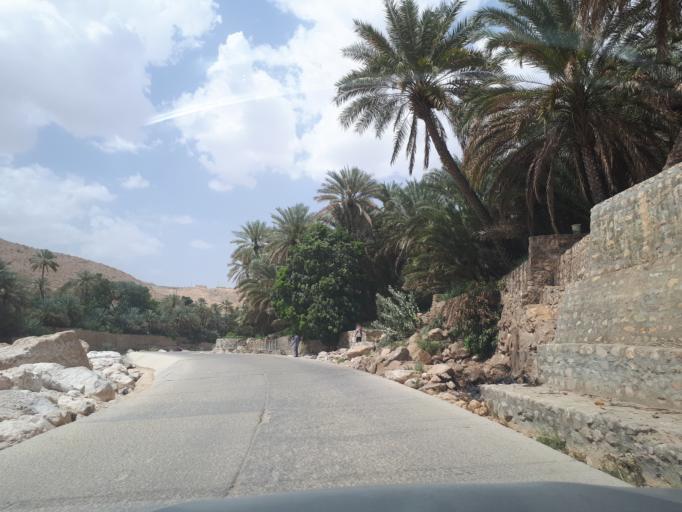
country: OM
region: Ash Sharqiyah
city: Badiyah
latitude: 22.6089
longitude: 59.0912
